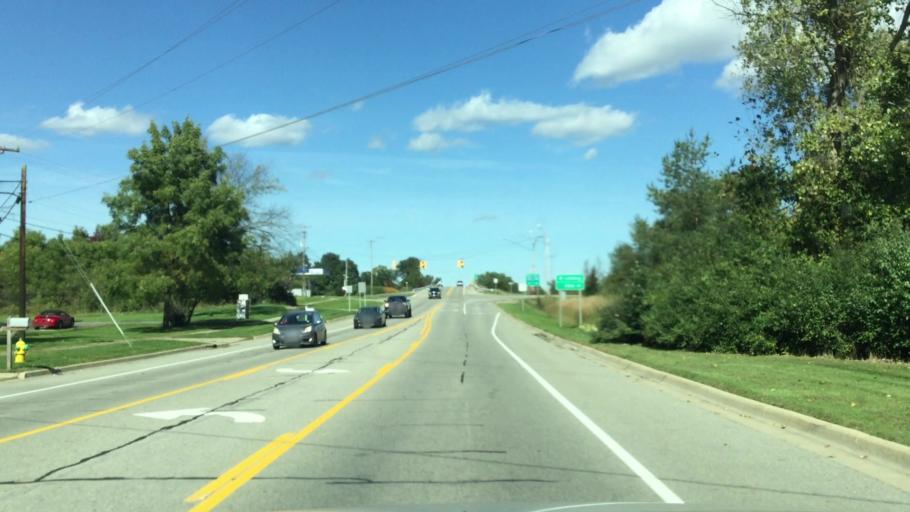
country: US
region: Michigan
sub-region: Genesee County
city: Swartz Creek
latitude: 42.9624
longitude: -83.8307
